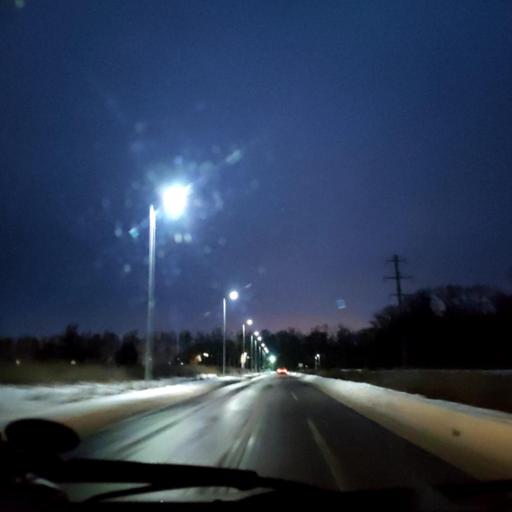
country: RU
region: Voronezj
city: Podgornoye
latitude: 51.7878
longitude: 39.1870
